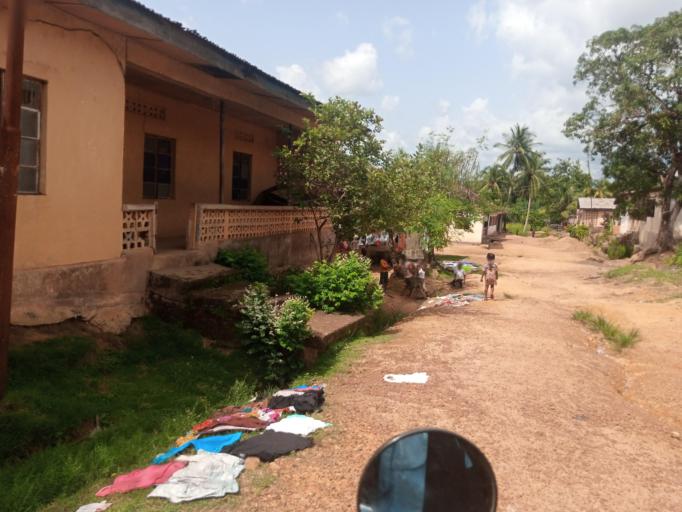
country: SL
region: Southern Province
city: Bo
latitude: 7.9770
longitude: -11.7336
